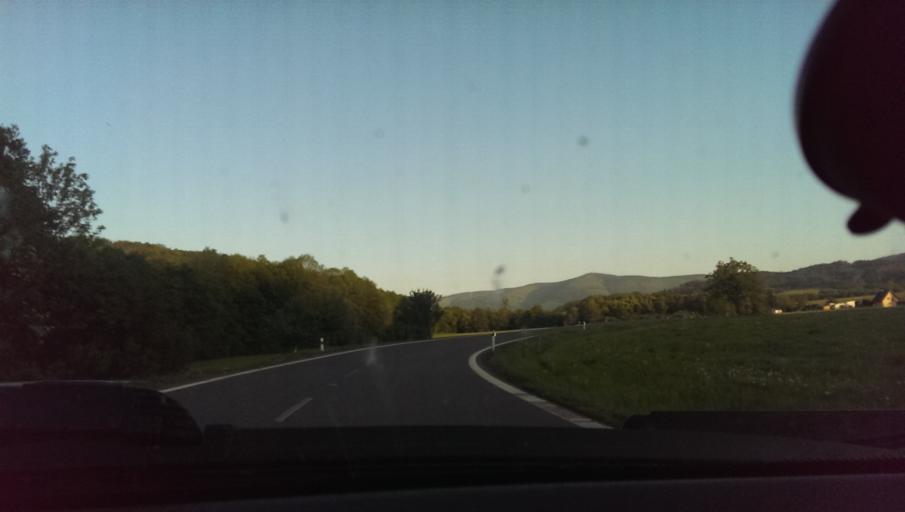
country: CZ
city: Lichnov (o. Novy Jicin)
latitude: 49.5709
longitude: 18.1854
